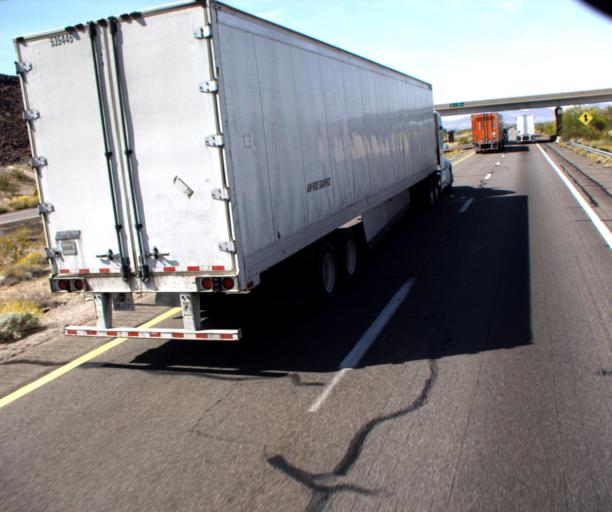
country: US
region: Arizona
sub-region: La Paz County
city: Quartzsite
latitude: 33.6794
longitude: -114.0831
